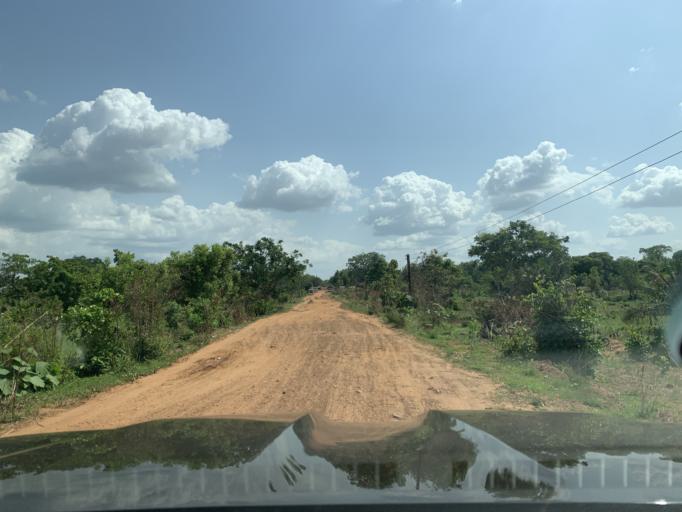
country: TG
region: Kara
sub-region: Prefecture de Bassar
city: Bassar
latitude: 9.3822
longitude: 0.5605
